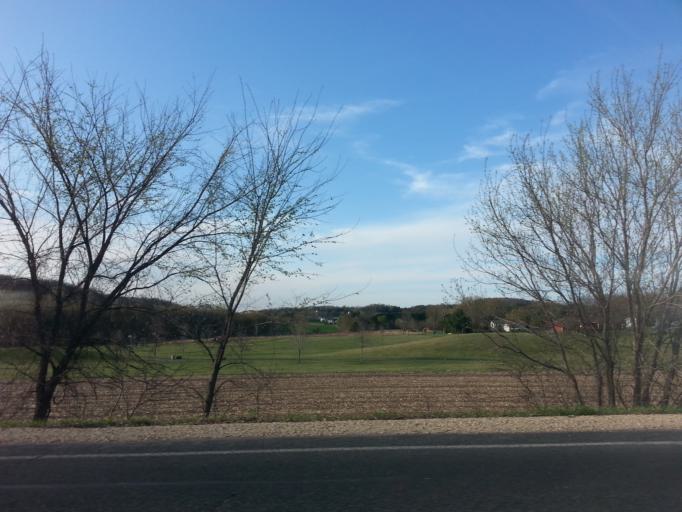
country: US
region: Wisconsin
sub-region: Pierce County
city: River Falls
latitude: 44.8626
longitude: -92.6450
